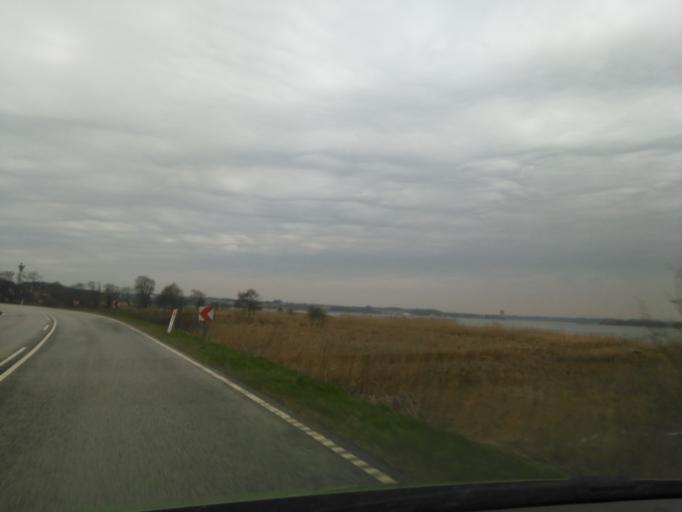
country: DK
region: North Denmark
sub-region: Mariagerfjord Kommune
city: Hadsund
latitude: 56.6922
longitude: 10.1058
